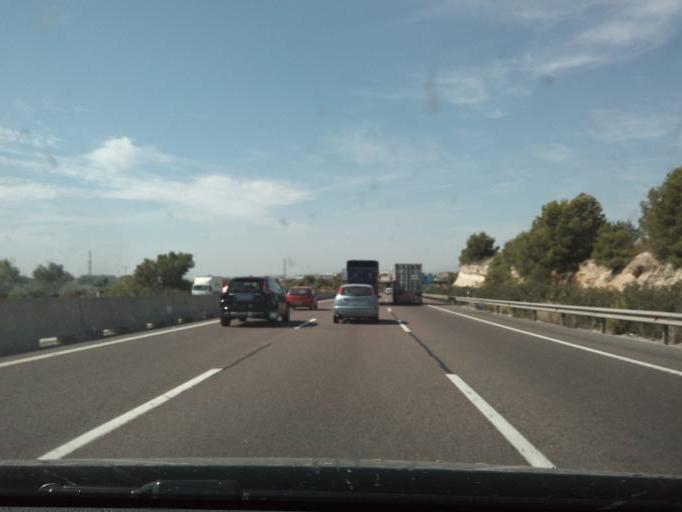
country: ES
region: Valencia
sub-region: Provincia de Valencia
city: Manises
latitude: 39.5293
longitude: -0.4643
